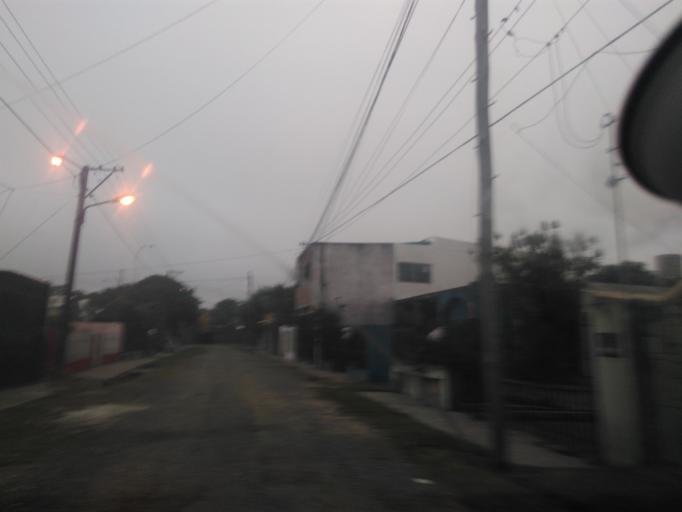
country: AR
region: Chaco
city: Resistencia
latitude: -27.4734
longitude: -58.9891
